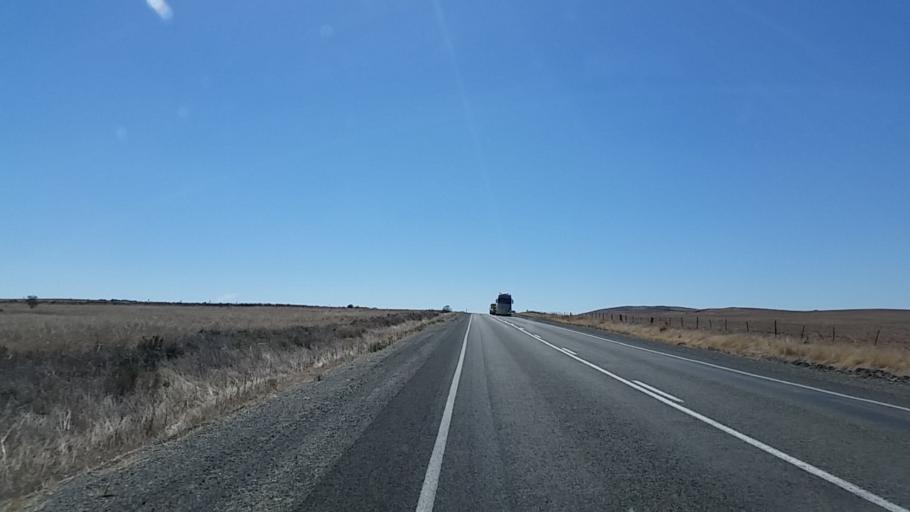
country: AU
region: South Australia
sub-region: Northern Areas
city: Jamestown
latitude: -33.3342
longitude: 138.8909
